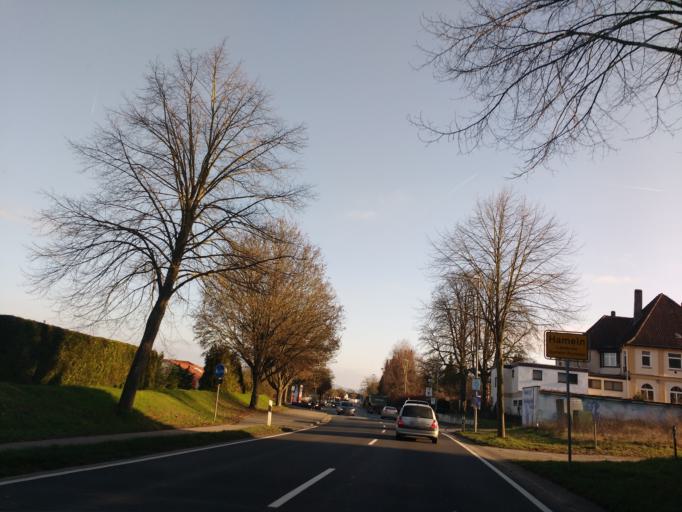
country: DE
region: Lower Saxony
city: Hameln
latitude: 52.1062
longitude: 9.3294
